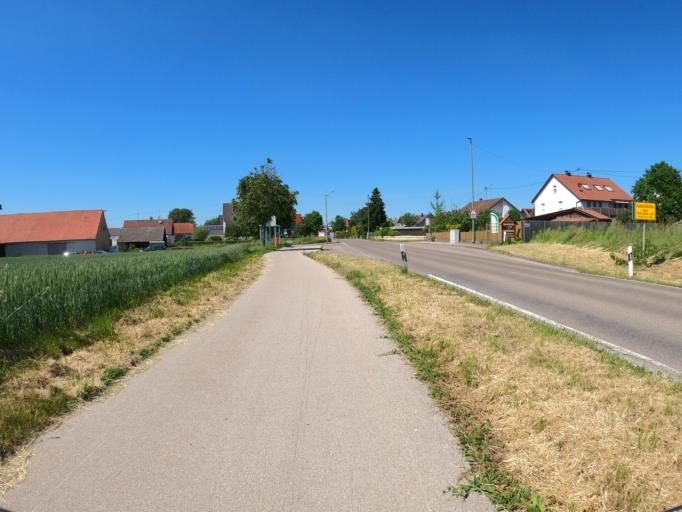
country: DE
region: Bavaria
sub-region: Swabia
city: Pfaffenhofen an der Roth
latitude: 48.3761
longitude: 10.1518
